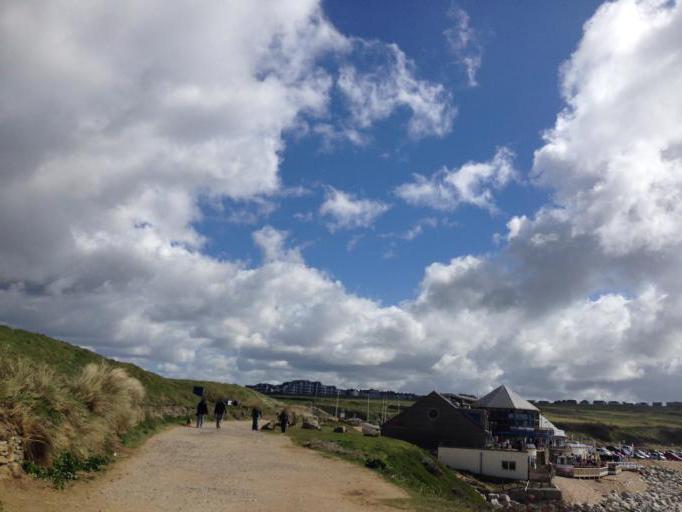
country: GB
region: England
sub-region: Cornwall
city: Newquay
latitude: 50.4200
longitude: -5.0978
